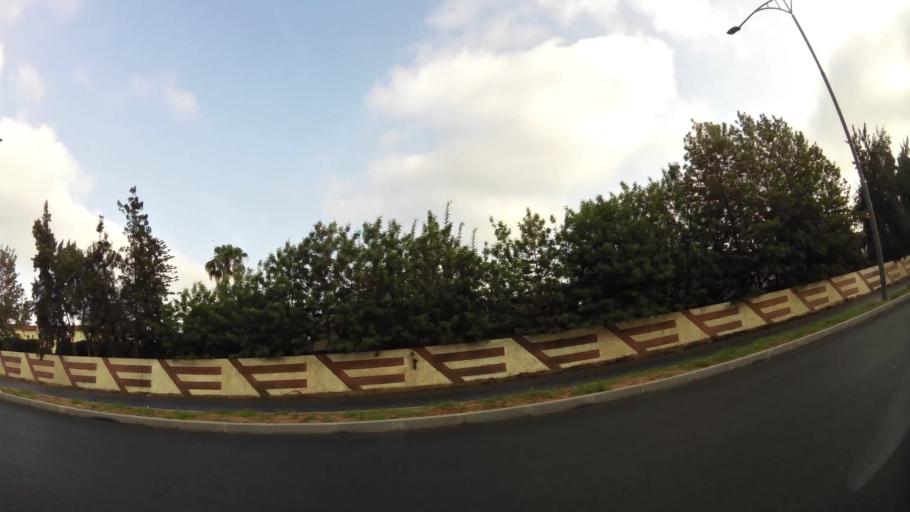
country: MA
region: Rabat-Sale-Zemmour-Zaer
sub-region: Rabat
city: Rabat
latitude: 33.9570
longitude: -6.8336
